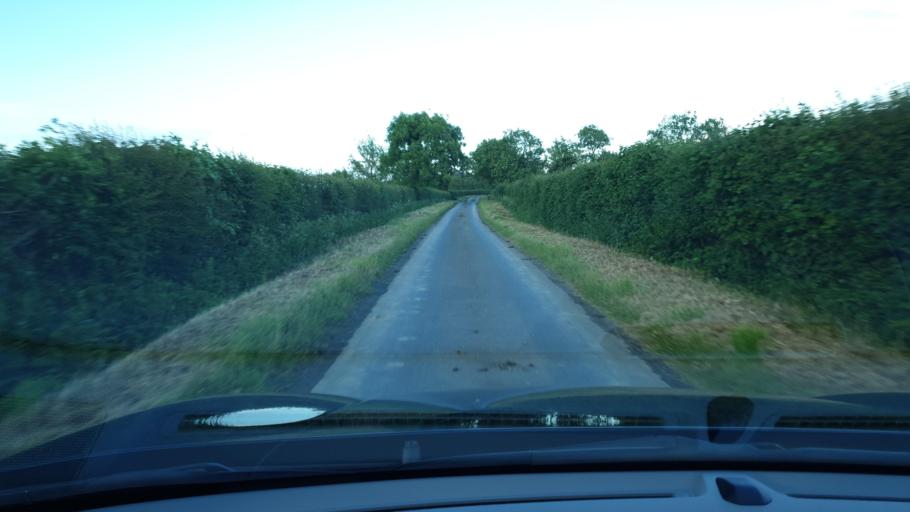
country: IE
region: Leinster
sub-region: An Mhi
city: Ashbourne
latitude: 53.4767
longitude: -6.3462
